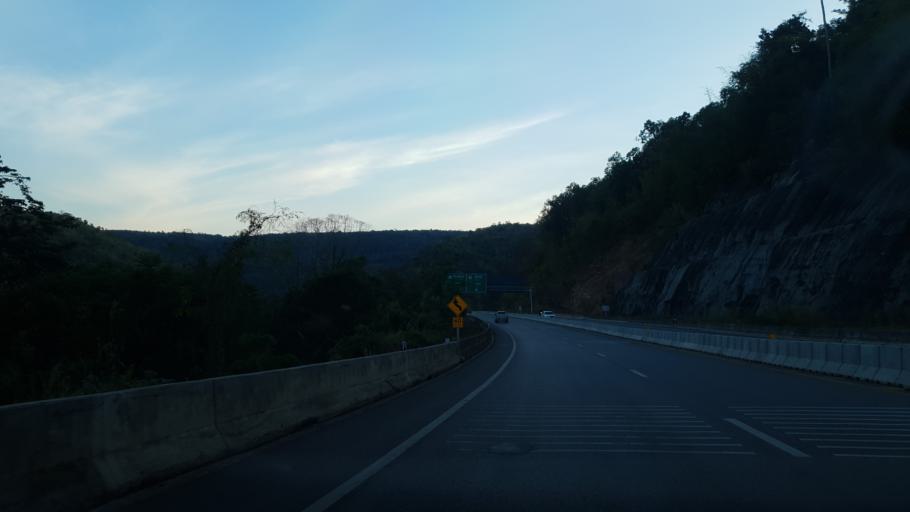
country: TH
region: Phitsanulok
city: Nakhon Thai
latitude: 16.8822
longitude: 100.7999
